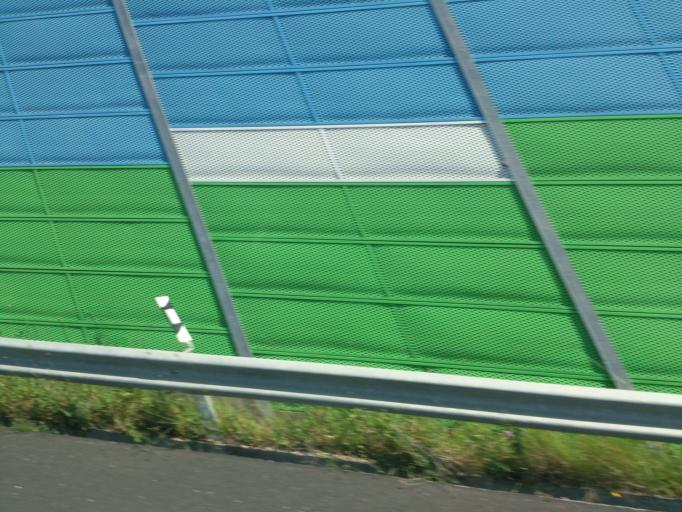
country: PT
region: Lisbon
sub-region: Mafra
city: Malveira
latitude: 38.9360
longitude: -9.2894
